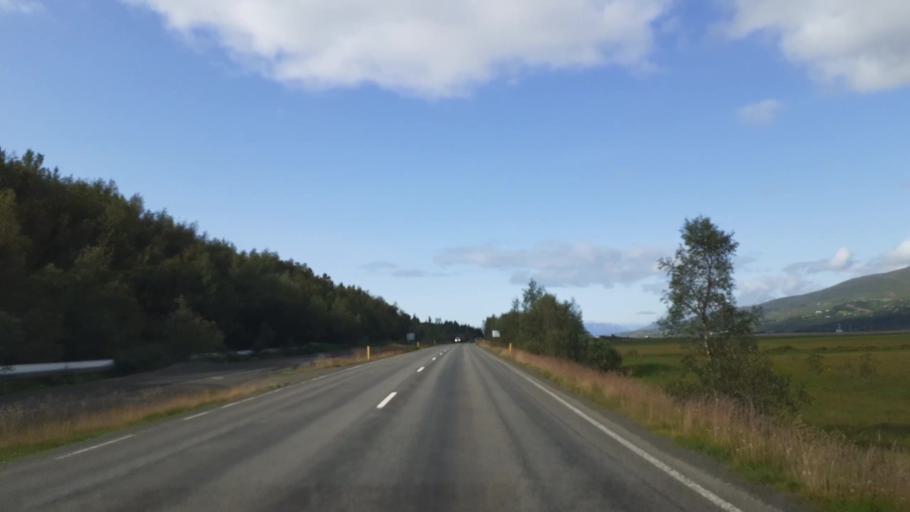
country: IS
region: Northeast
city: Akureyri
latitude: 65.6409
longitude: -18.0726
